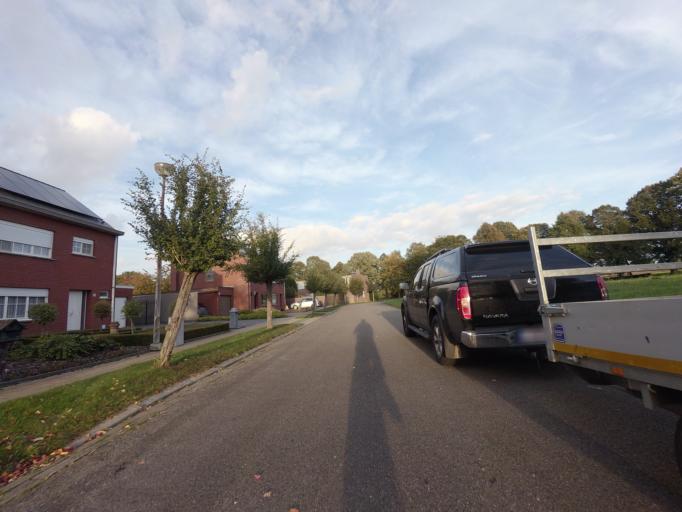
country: BE
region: Flanders
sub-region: Provincie Antwerpen
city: Willebroek
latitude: 51.0499
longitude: 4.3853
